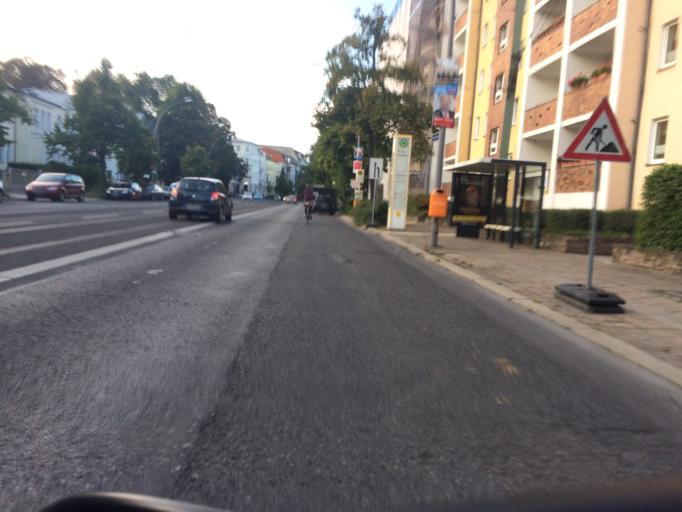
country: DE
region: Berlin
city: Pankow
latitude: 52.5754
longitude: 13.3990
